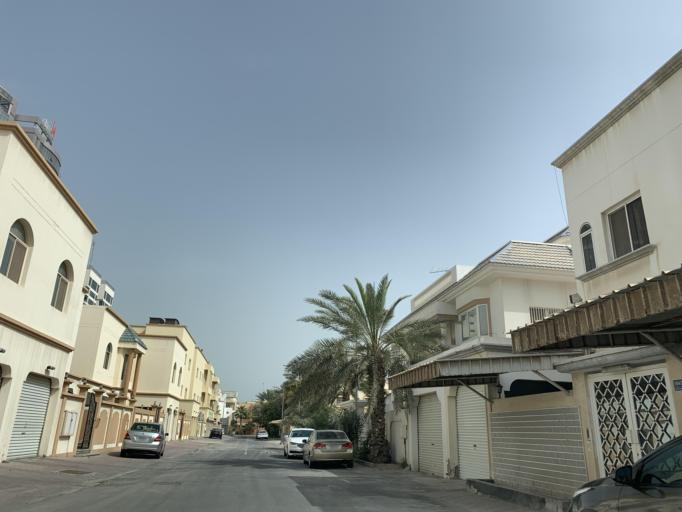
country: BH
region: Manama
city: Manama
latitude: 26.2132
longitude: 50.6129
